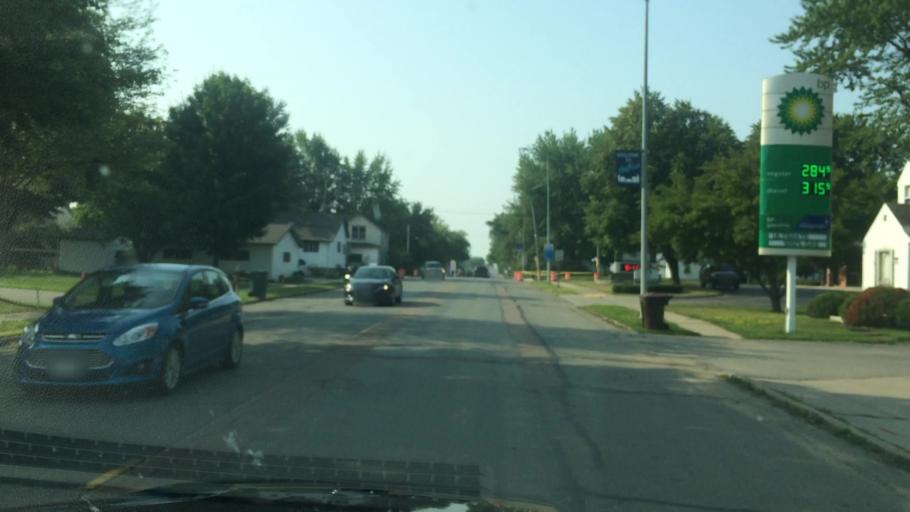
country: US
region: Wisconsin
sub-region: Marathon County
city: Stratford
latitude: 44.8039
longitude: -90.0792
